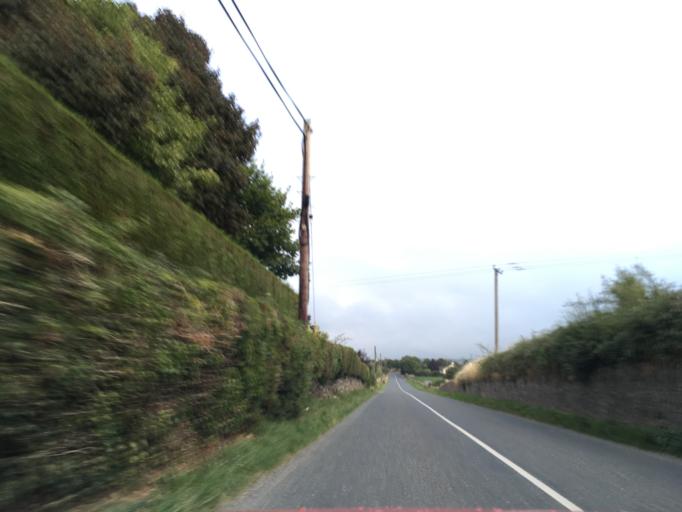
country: IE
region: Munster
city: Cashel
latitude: 52.4972
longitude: -7.9777
